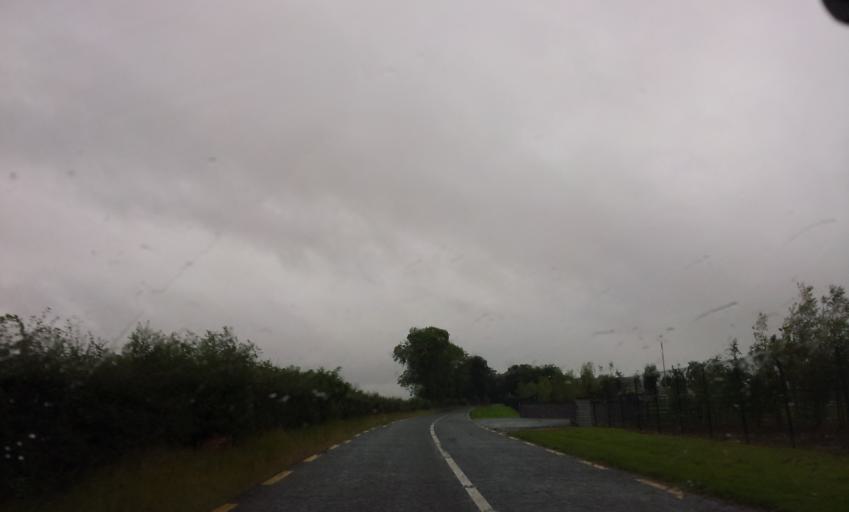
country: IE
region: Munster
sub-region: County Cork
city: Mallow
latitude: 52.1552
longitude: -8.6059
